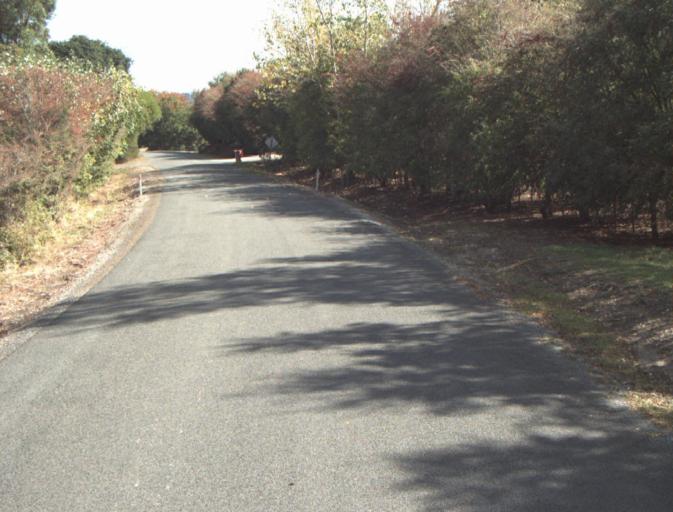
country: AU
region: Tasmania
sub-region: Launceston
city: Mayfield
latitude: -41.2409
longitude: 147.2324
